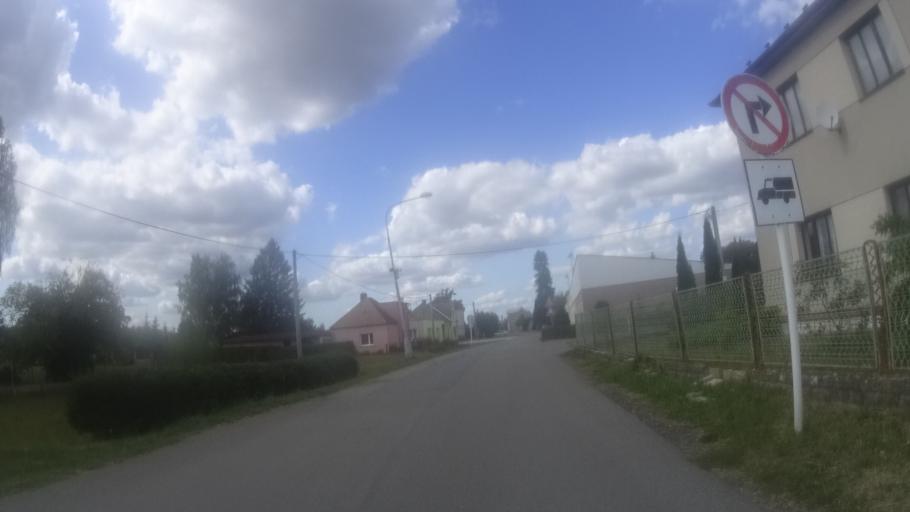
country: CZ
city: Borohradek
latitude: 50.0743
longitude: 16.1337
